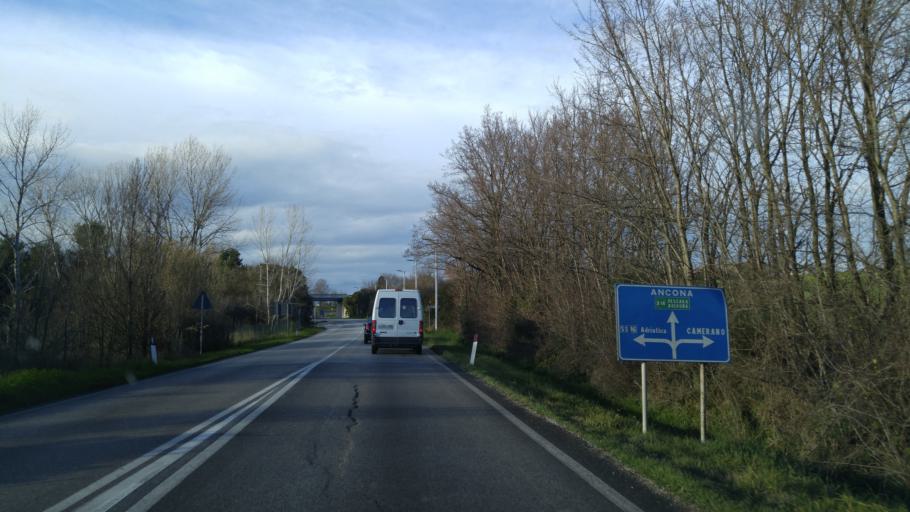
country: IT
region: The Marches
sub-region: Provincia di Ancona
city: Camerano
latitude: 43.5192
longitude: 13.5371
